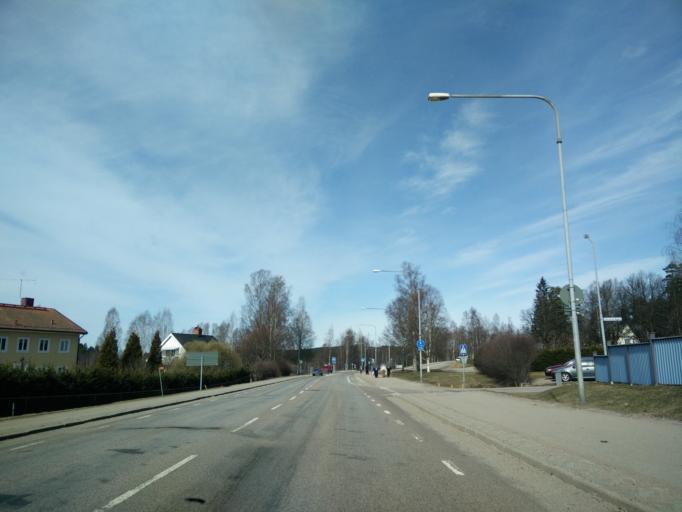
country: SE
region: Vaermland
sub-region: Hagfors Kommun
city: Hagfors
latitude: 60.0372
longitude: 13.7050
